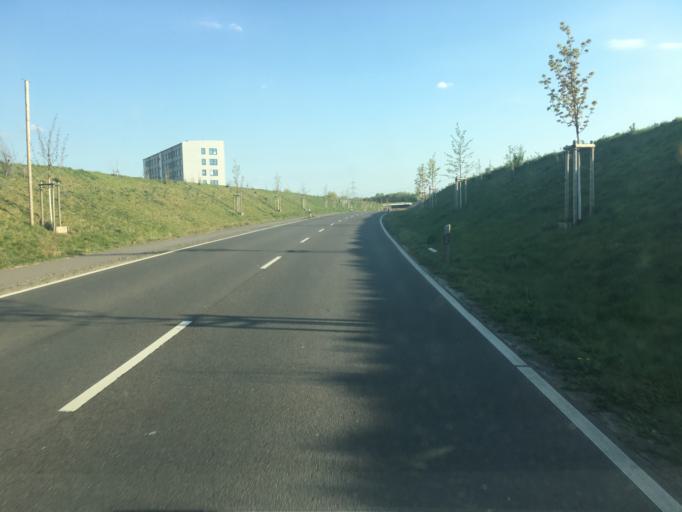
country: DE
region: North Rhine-Westphalia
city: Monheim am Rhein
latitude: 51.0362
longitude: 6.9154
